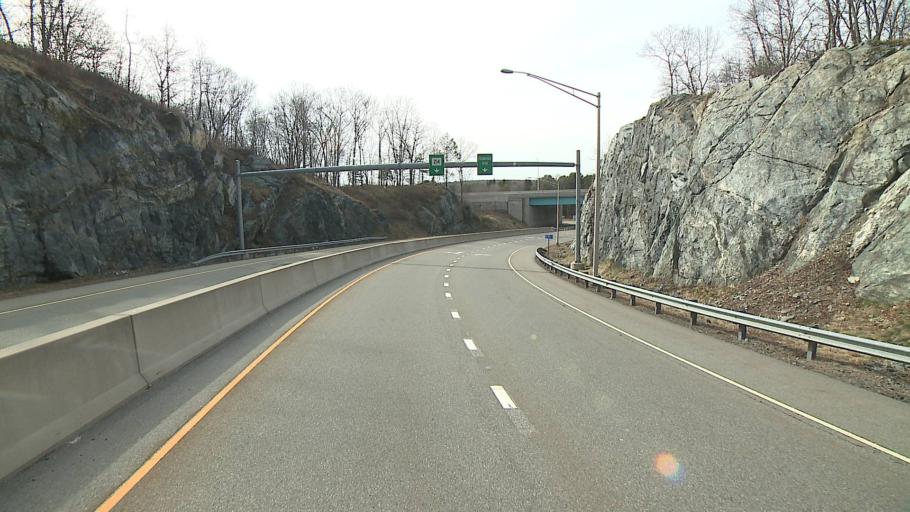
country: US
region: Connecticut
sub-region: New London County
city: Preston City
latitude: 41.4714
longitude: -71.9497
